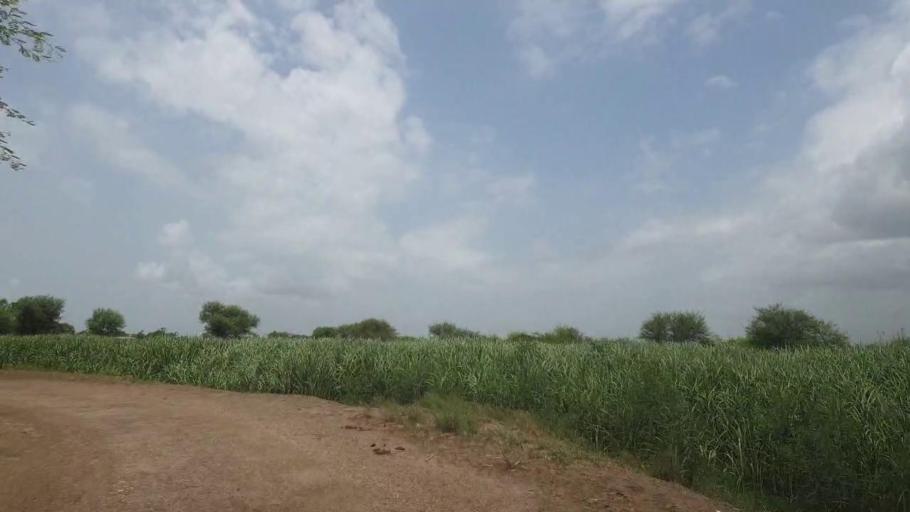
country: PK
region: Sindh
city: Badin
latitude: 24.6613
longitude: 68.9448
